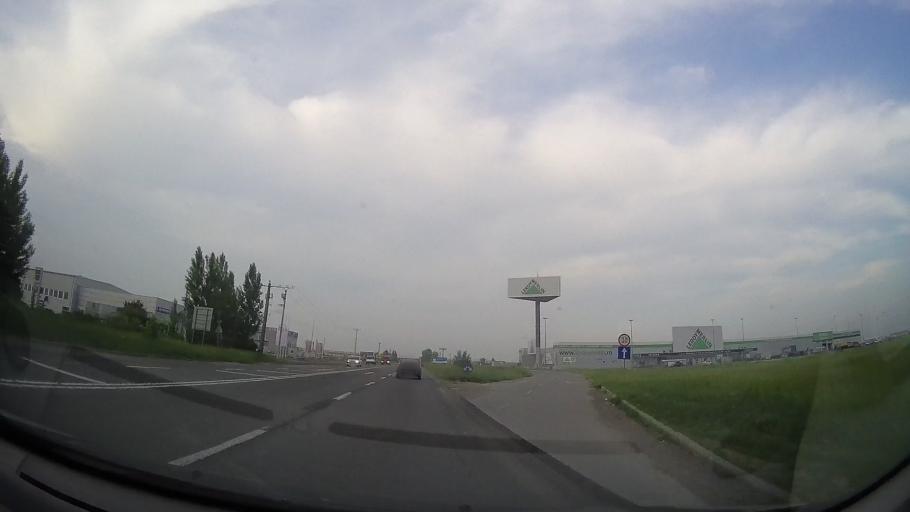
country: RO
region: Timis
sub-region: Comuna Giroc
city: Chisoda
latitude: 45.7048
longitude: 21.1855
